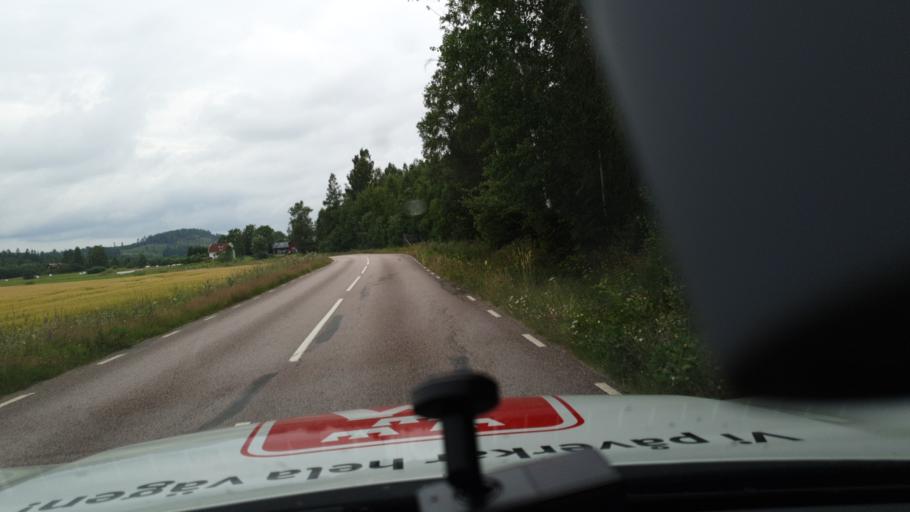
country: SE
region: Vaermland
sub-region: Sunne Kommun
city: Sunne
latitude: 59.7888
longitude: 13.2320
